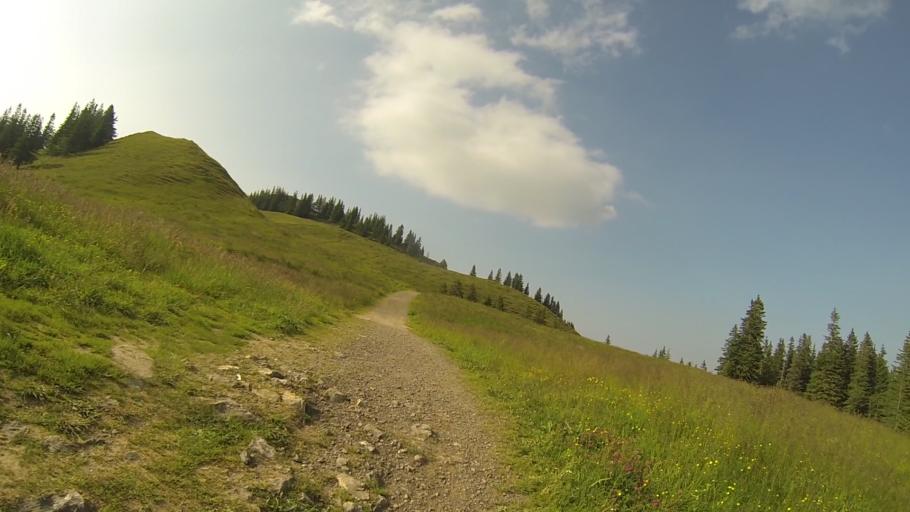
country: DE
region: Bavaria
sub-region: Swabia
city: Nesselwang
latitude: 47.5947
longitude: 10.4978
